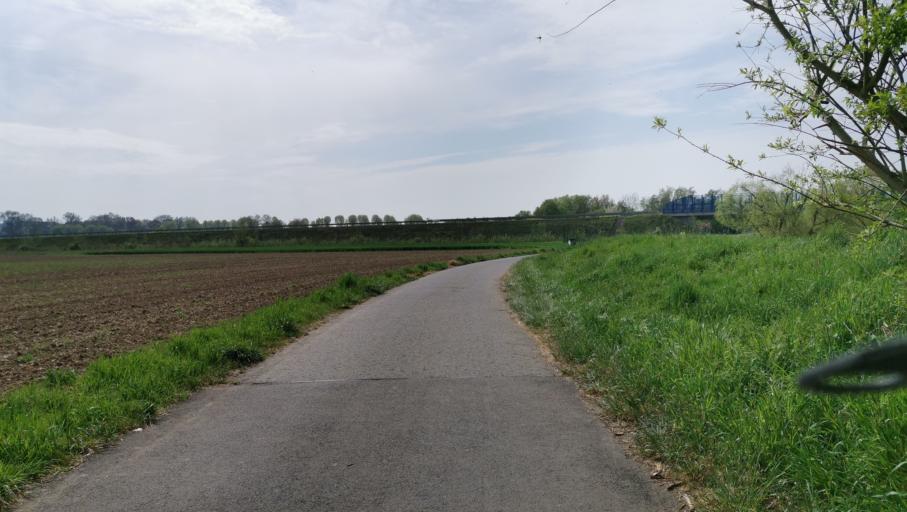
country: DE
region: Hesse
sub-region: Regierungsbezirk Darmstadt
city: Karben
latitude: 50.2417
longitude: 8.7601
